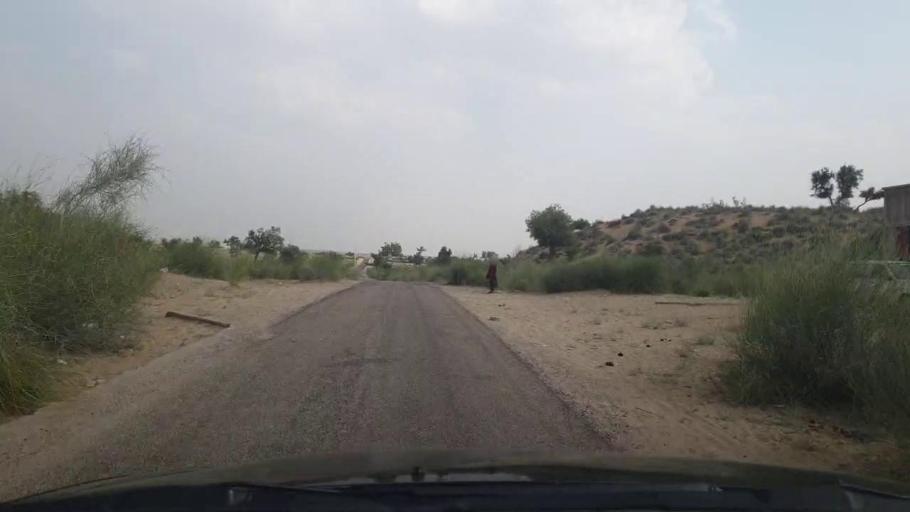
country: PK
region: Sindh
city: Islamkot
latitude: 25.0218
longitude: 70.5913
